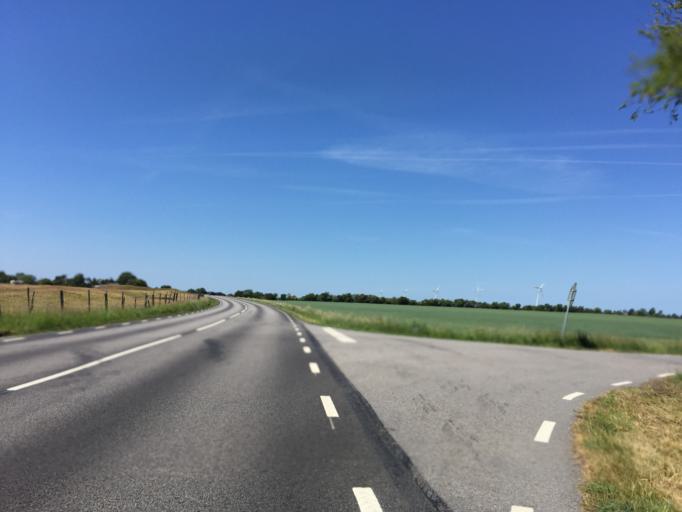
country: SE
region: Skane
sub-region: Trelleborgs Kommun
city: Skare
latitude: 55.3752
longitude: 13.0639
